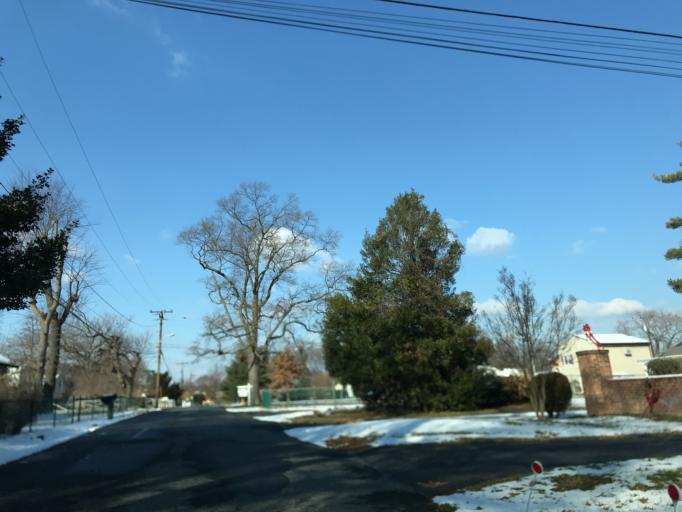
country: US
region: Maryland
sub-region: Baltimore County
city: Bowleys Quarters
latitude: 39.3167
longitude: -76.3775
